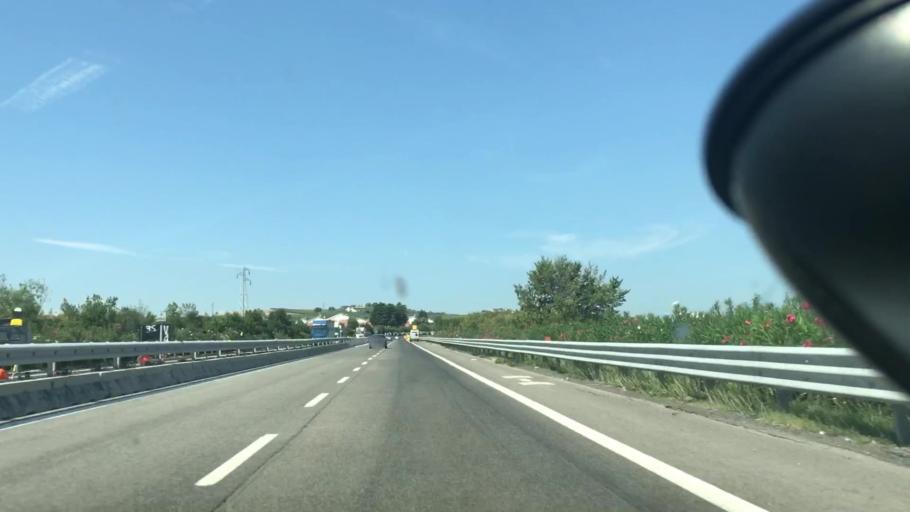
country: IT
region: Abruzzo
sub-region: Provincia di Chieti
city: San Salvo
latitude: 42.0626
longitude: 14.7344
